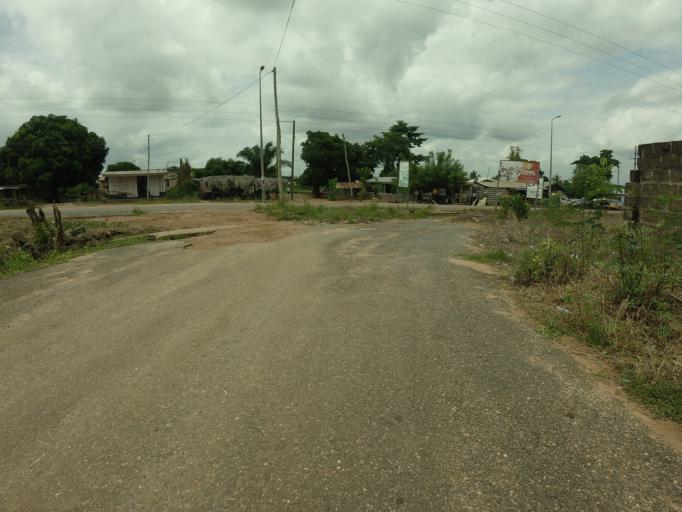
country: GH
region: Volta
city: Ho
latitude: 6.5894
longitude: 0.4790
